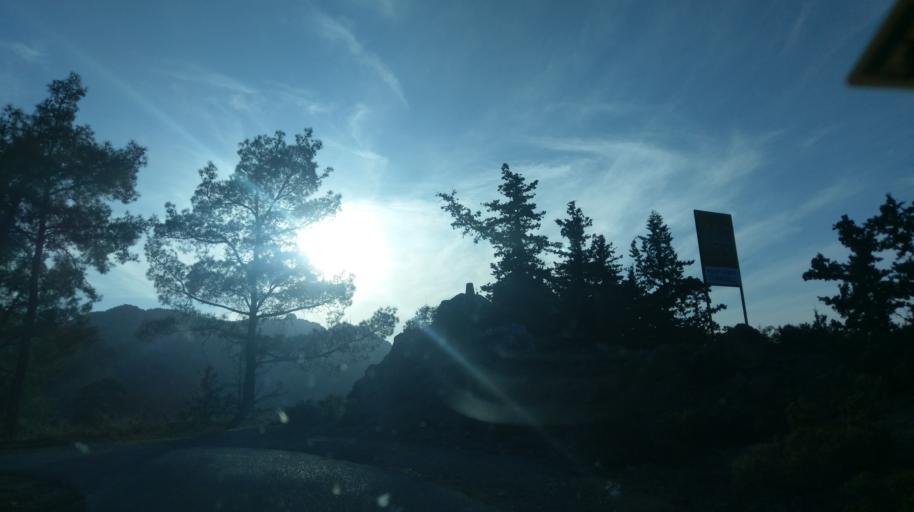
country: CY
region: Ammochostos
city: Lefkonoiko
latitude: 35.3094
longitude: 33.5739
